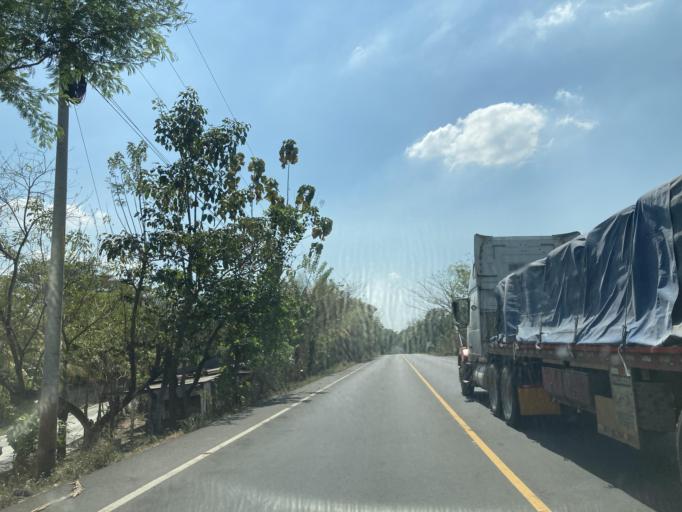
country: GT
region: Escuintla
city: Guanagazapa
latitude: 14.2052
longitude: -90.7151
